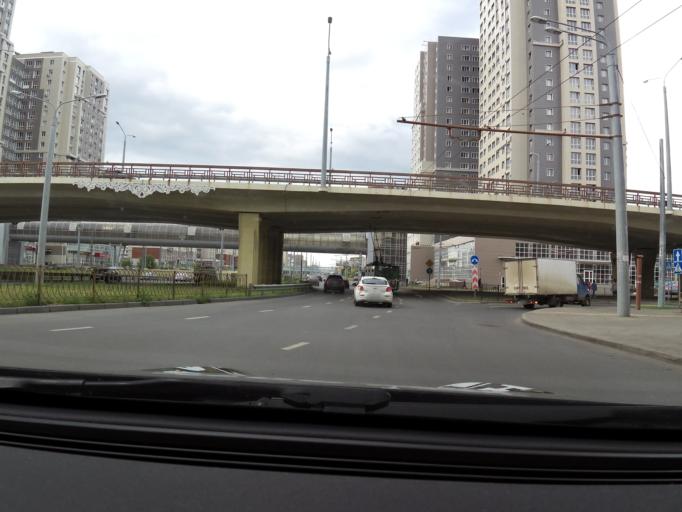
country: RU
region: Tatarstan
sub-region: Gorod Kazan'
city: Kazan
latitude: 55.8189
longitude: 49.1342
